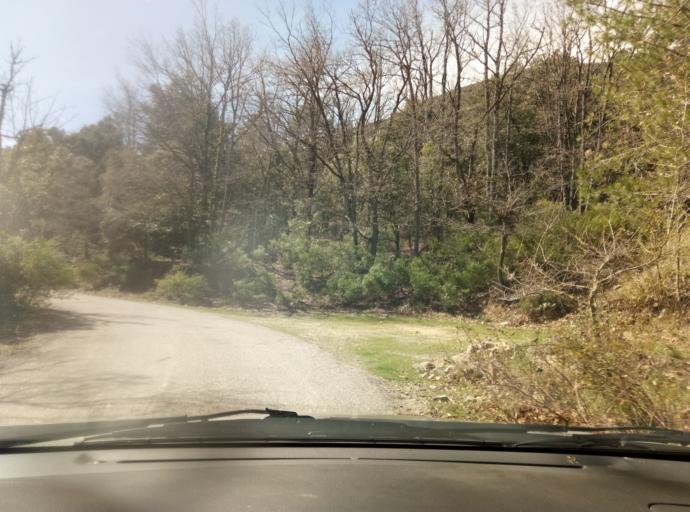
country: ES
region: Catalonia
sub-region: Provincia de Tarragona
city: Vimbodi
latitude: 41.3481
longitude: 1.0581
